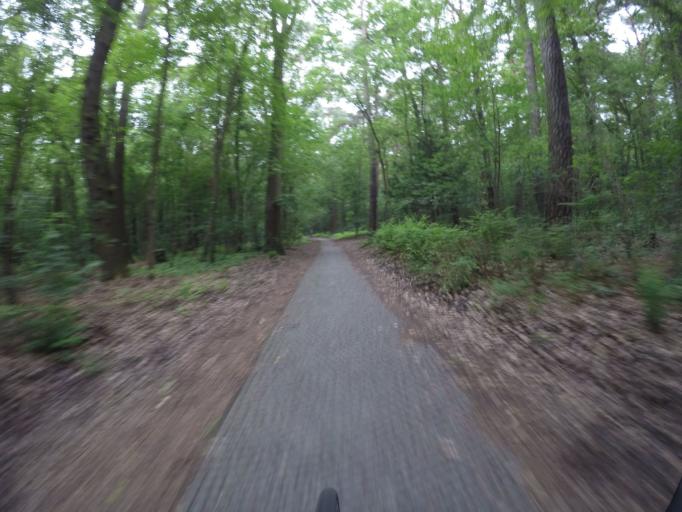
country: DE
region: Berlin
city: Wittenau
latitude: 52.5988
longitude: 13.3133
